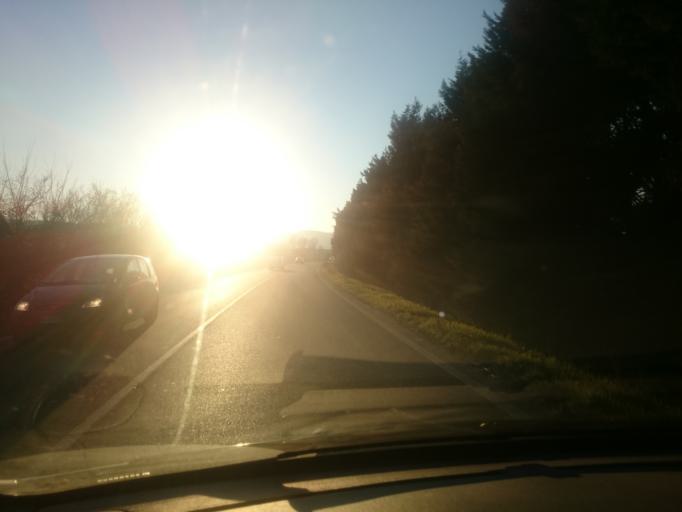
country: IT
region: Emilia-Romagna
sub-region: Provincia di Reggio Emilia
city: Scandiano
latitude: 44.5920
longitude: 10.7014
